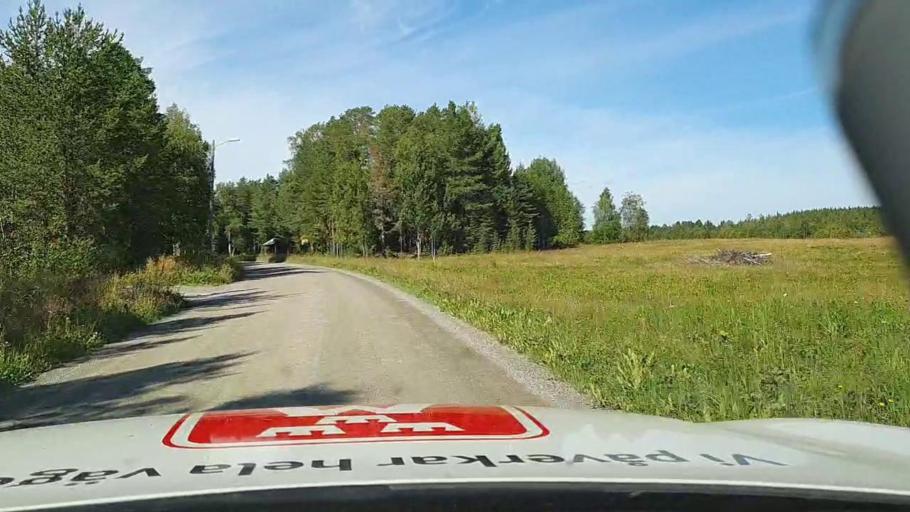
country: SE
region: Jaemtland
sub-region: Stroemsunds Kommun
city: Stroemsund
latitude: 63.6913
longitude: 15.3814
